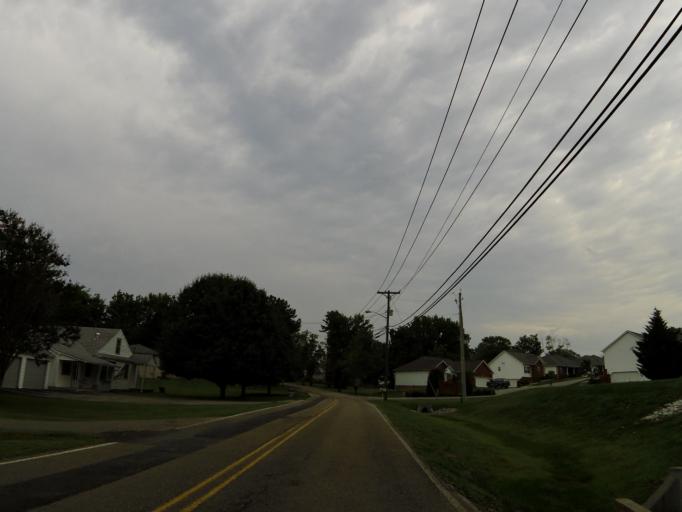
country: US
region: Tennessee
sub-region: Knox County
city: Knoxville
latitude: 35.9281
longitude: -83.8682
